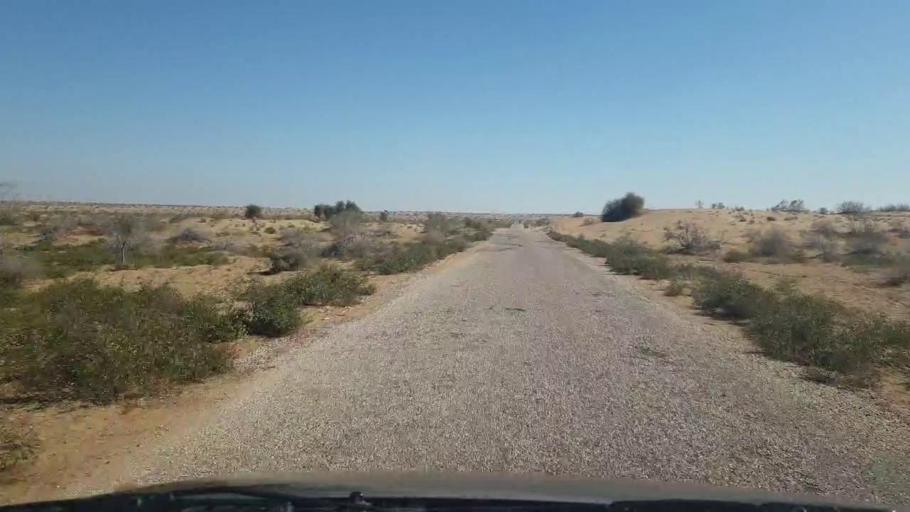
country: PK
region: Sindh
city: Bozdar
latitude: 27.0133
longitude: 68.7880
